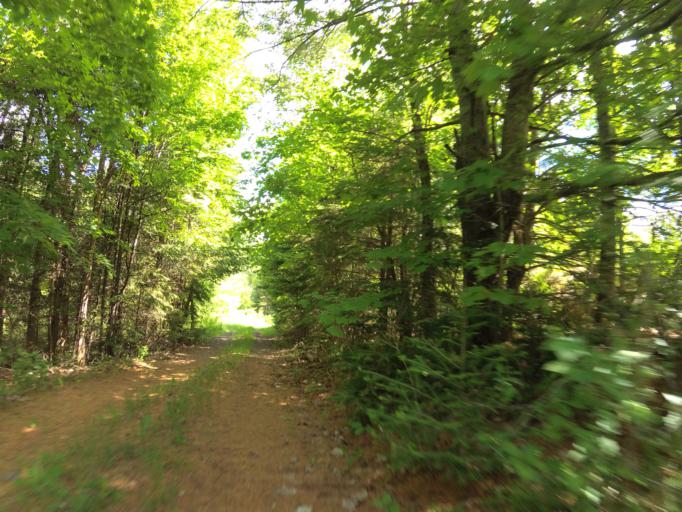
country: CA
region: Ontario
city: Renfrew
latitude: 45.0533
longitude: -76.7576
